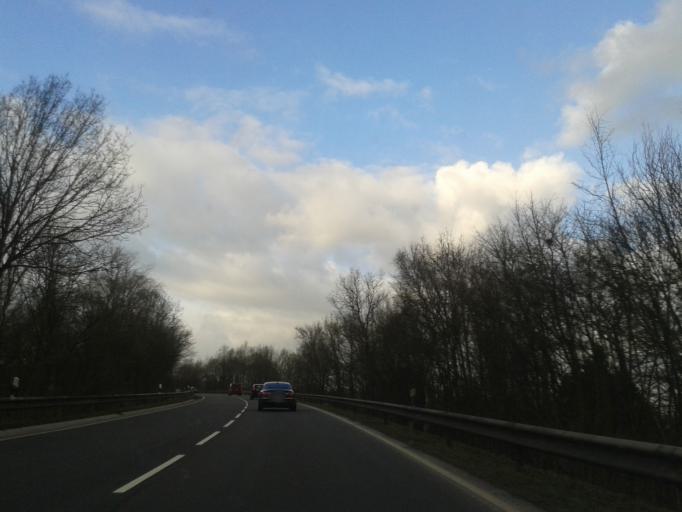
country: DE
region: Lower Saxony
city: Upgant-Schott
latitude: 53.5218
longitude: 7.2806
